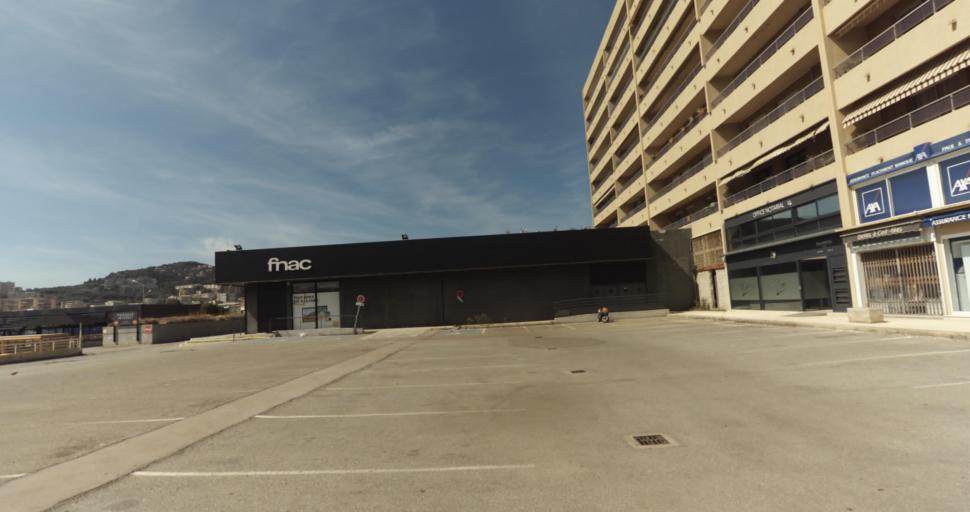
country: FR
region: Corsica
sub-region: Departement de la Corse-du-Sud
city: Ajaccio
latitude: 41.9328
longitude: 8.7483
